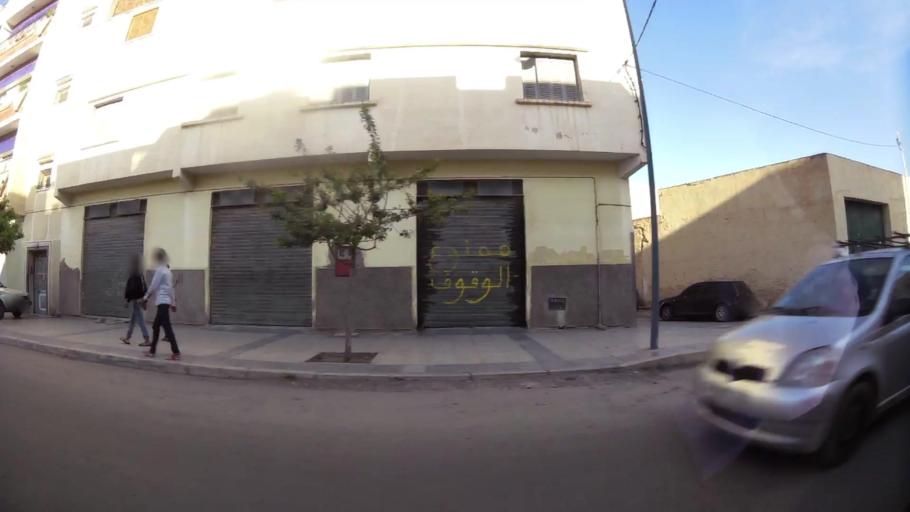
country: MA
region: Oriental
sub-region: Oujda-Angad
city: Oujda
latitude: 34.6962
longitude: -1.9104
